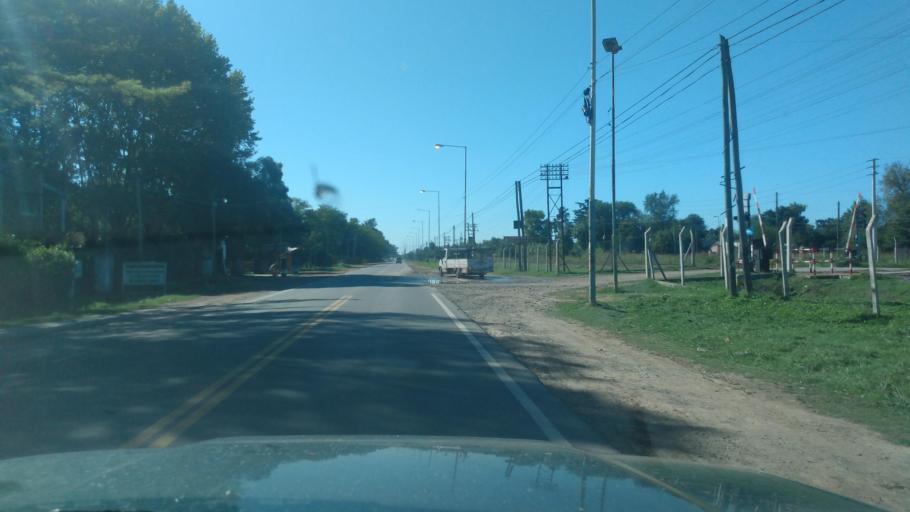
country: AR
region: Buenos Aires
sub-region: Partido de General Rodriguez
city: General Rodriguez
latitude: -34.5995
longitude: -58.9923
